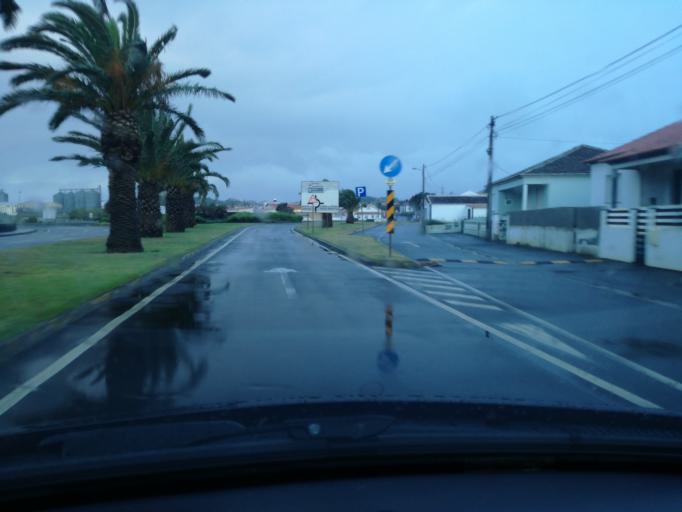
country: PT
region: Azores
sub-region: Praia da Vitoria
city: Praia da Vitoria
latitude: 38.7116
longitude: -27.0616
